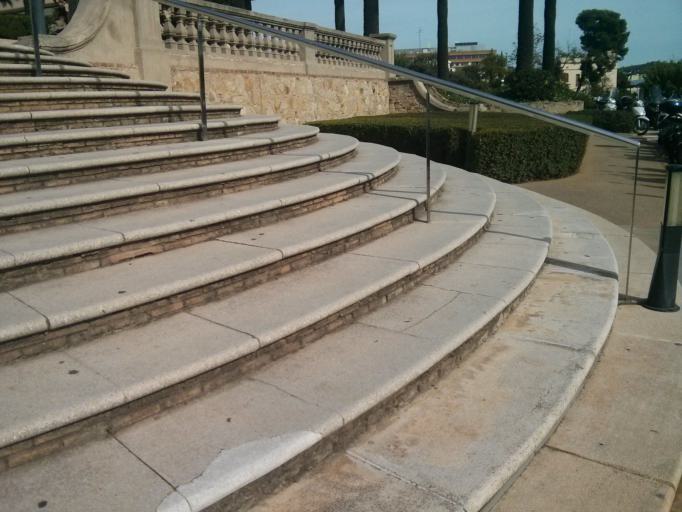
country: ES
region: Catalonia
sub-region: Provincia de Barcelona
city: Sarria-Sant Gervasi
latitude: 41.4060
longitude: 2.1277
